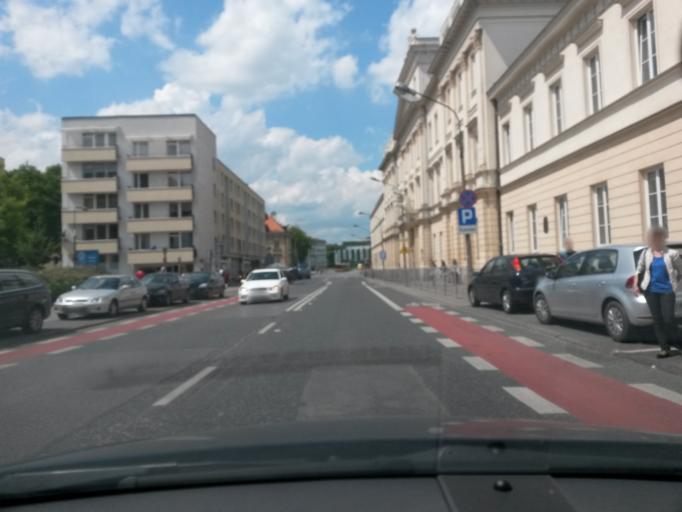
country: PL
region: Masovian Voivodeship
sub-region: Warszawa
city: Warsaw
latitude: 52.2481
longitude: 21.0078
